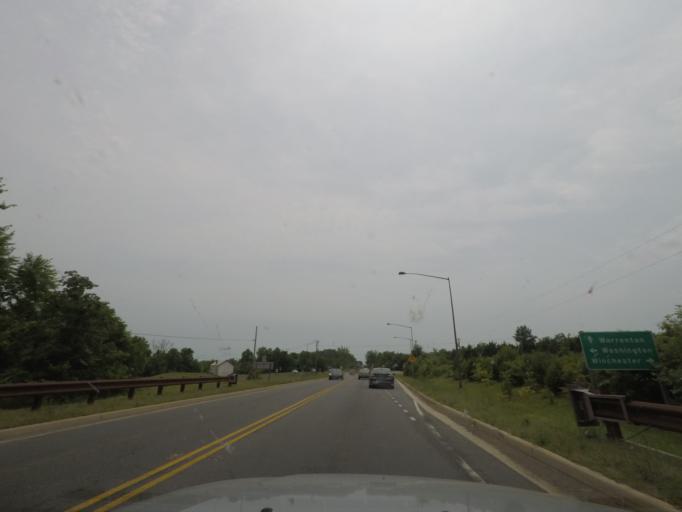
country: US
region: Virginia
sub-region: Prince William County
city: Bull Run Mountain Estates
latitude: 38.9707
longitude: -77.6227
